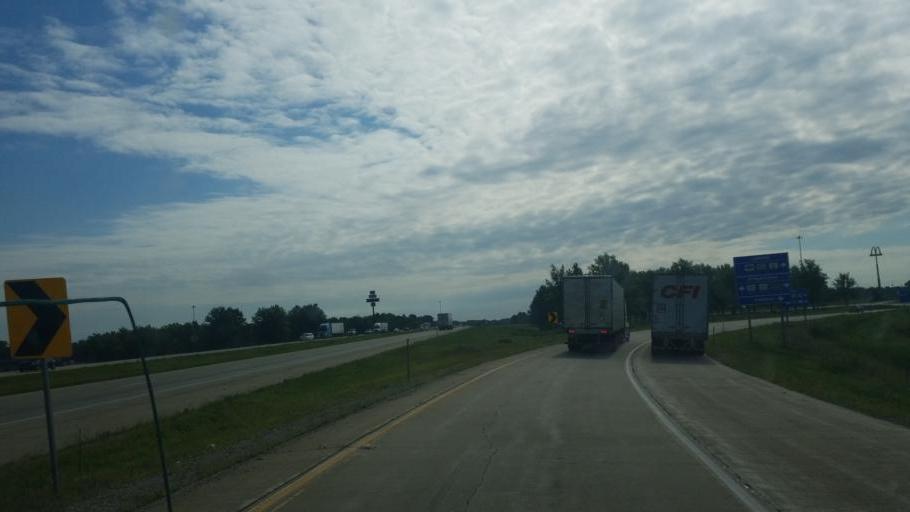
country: US
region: Illinois
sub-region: Clark County
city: Marshall
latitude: 39.4207
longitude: -87.6977
